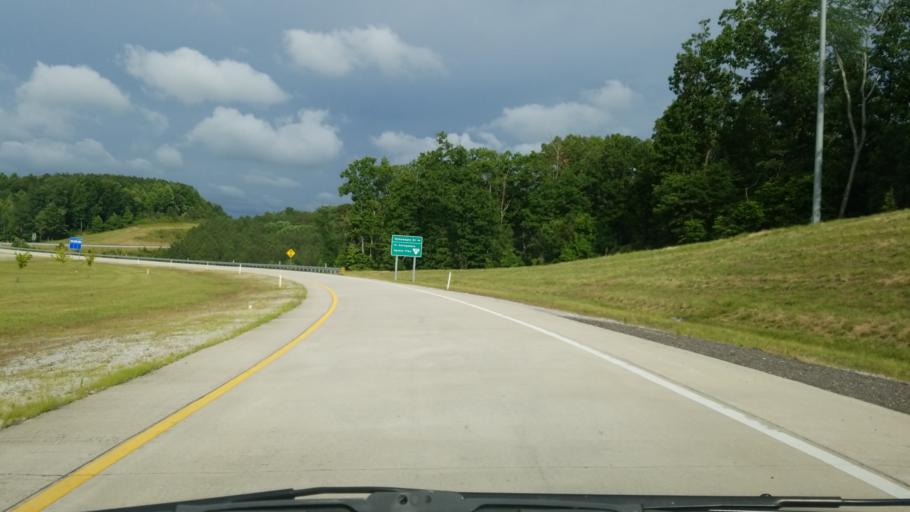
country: US
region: Tennessee
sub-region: Hamilton County
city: Harrison
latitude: 35.0762
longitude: -85.1105
